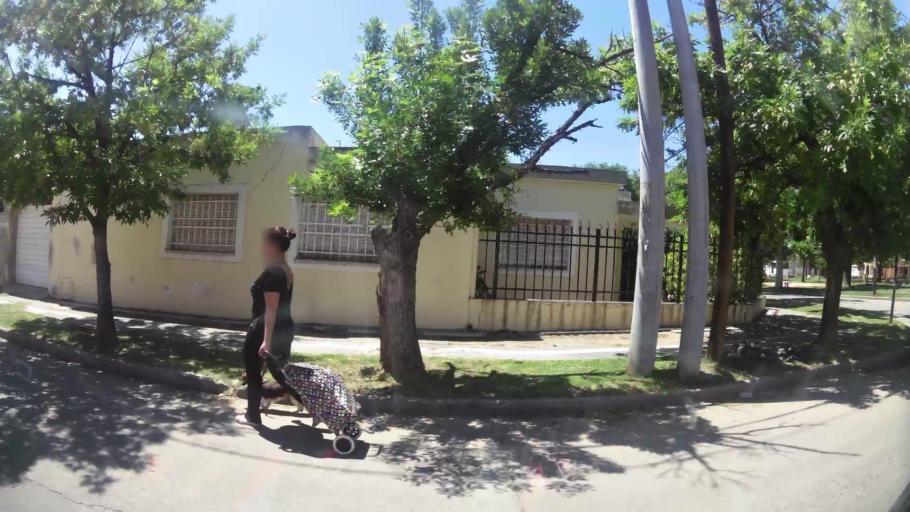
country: AR
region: Cordoba
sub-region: Departamento de Capital
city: Cordoba
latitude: -31.4125
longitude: -64.2135
